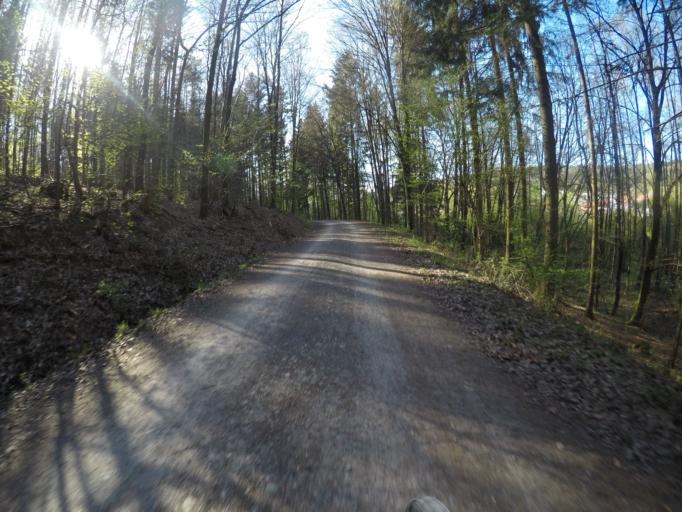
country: DE
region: Baden-Wuerttemberg
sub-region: Regierungsbezirk Stuttgart
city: Schlaitdorf
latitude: 48.6216
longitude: 9.2159
